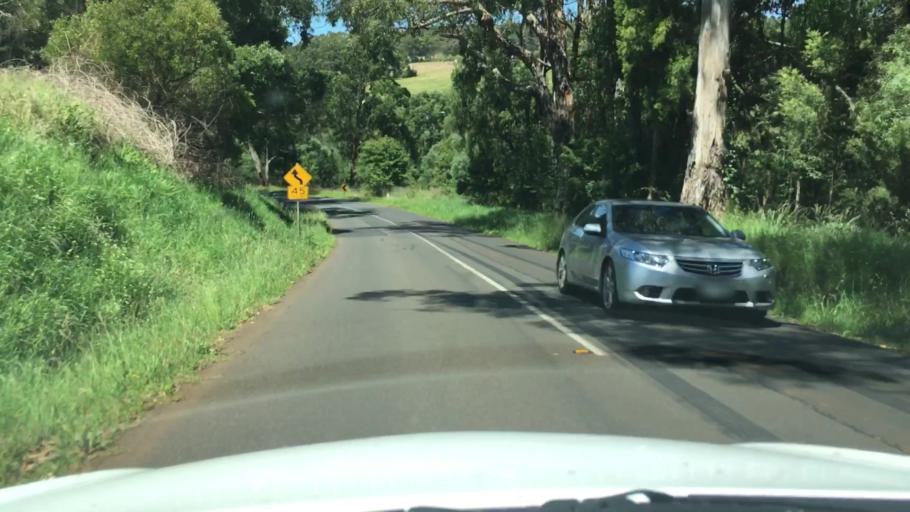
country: AU
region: Victoria
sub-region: Yarra Ranges
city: Mount Evelyn
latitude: -37.8072
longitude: 145.4073
